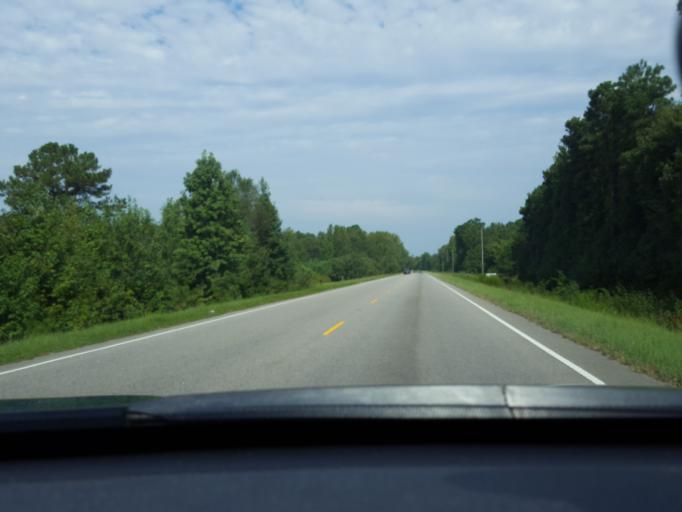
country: US
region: North Carolina
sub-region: Washington County
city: Plymouth
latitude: 35.9040
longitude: -76.7123
